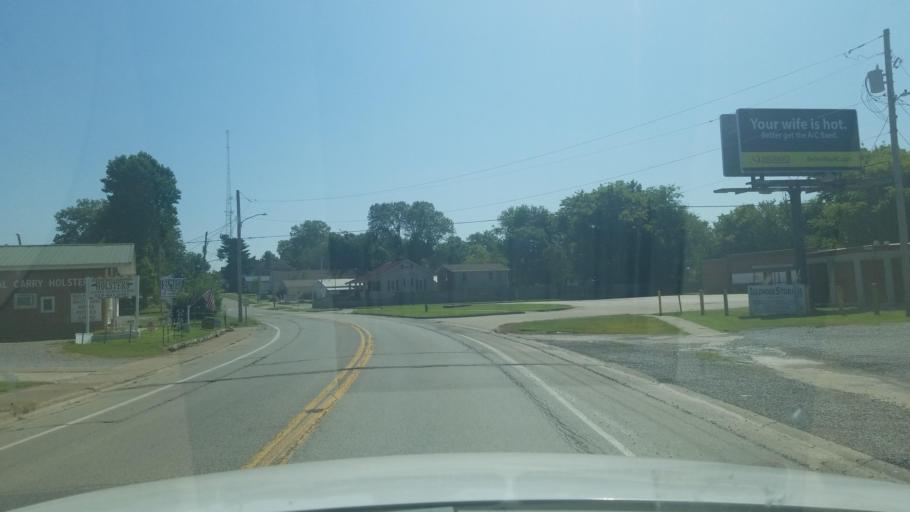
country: US
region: Illinois
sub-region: Saline County
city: Harrisburg
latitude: 37.7385
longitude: -88.5493
